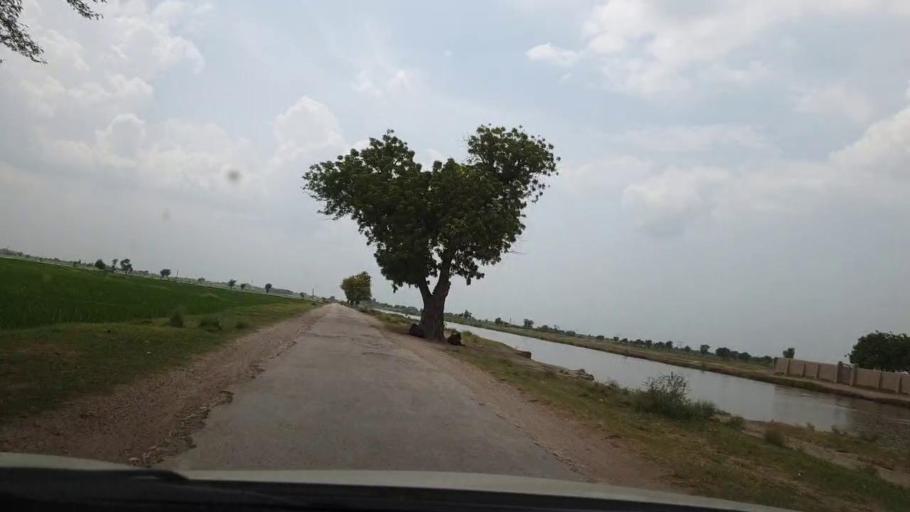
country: PK
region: Sindh
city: Goth Garelo
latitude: 27.4316
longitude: 68.1087
